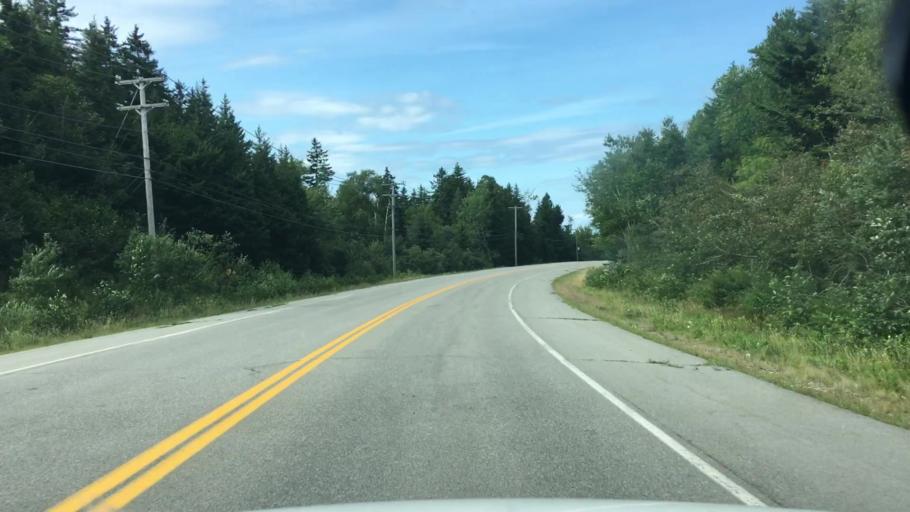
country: US
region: Maine
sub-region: Washington County
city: Eastport
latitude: 44.9292
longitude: -67.0260
